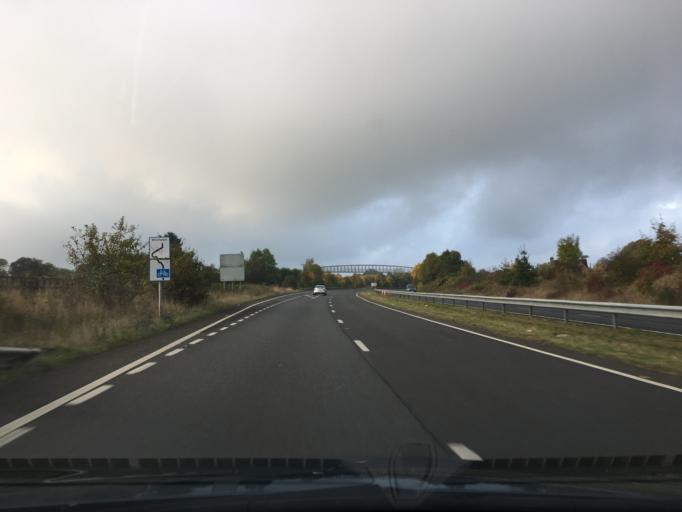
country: GB
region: England
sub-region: Hampshire
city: Kingsley
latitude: 51.1884
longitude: -0.8716
